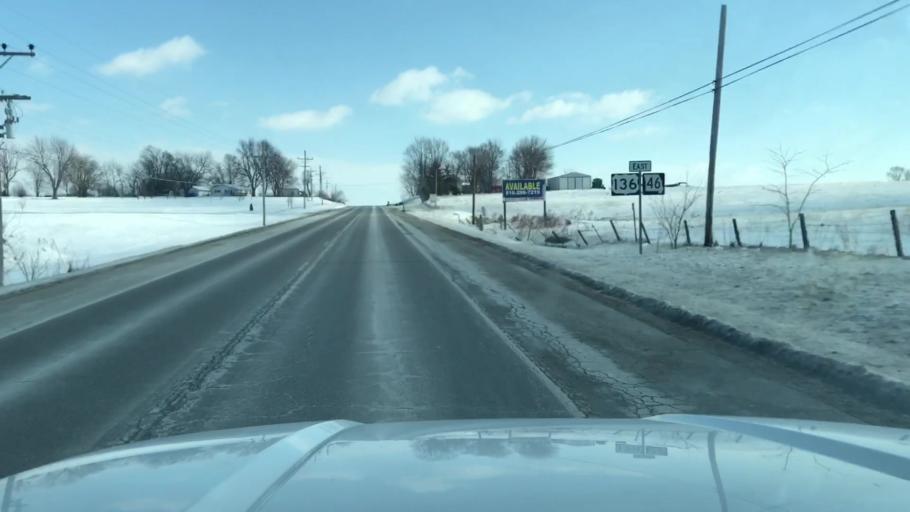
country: US
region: Missouri
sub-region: Nodaway County
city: Maryville
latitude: 40.3446
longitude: -94.7976
